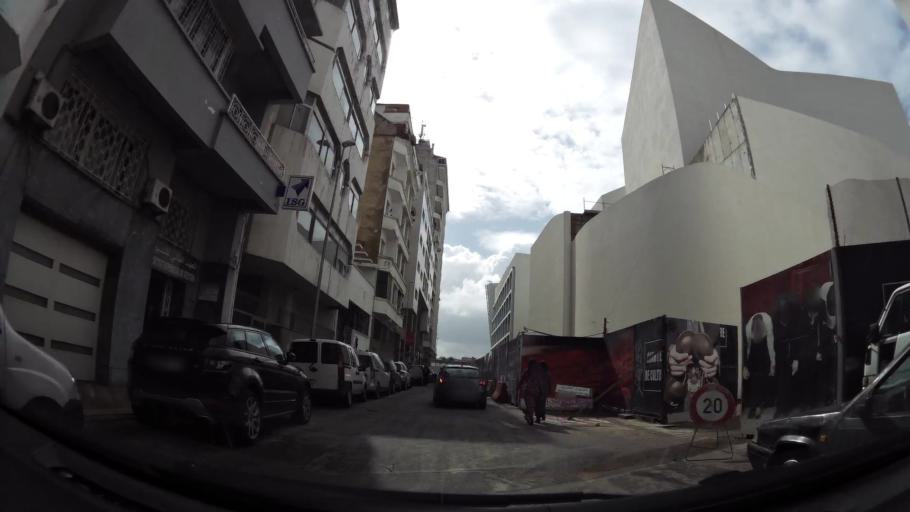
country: MA
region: Grand Casablanca
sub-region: Casablanca
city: Casablanca
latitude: 33.5930
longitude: -7.6219
